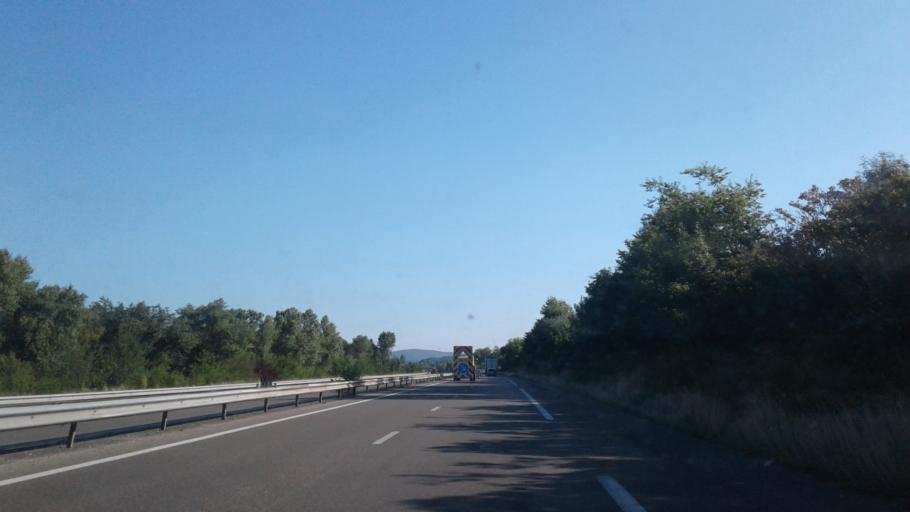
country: FR
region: Rhone-Alpes
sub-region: Departement de l'Ain
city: Priay
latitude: 46.0382
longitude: 5.3219
